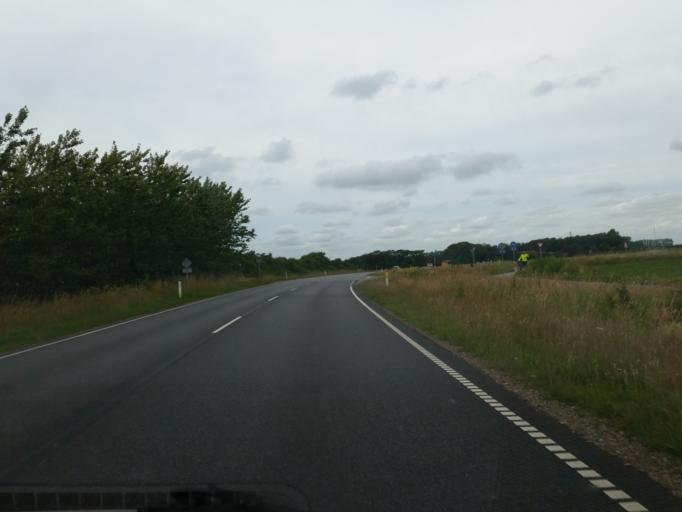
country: DK
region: South Denmark
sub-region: Esbjerg Kommune
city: Ribe
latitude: 55.2618
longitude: 8.7223
